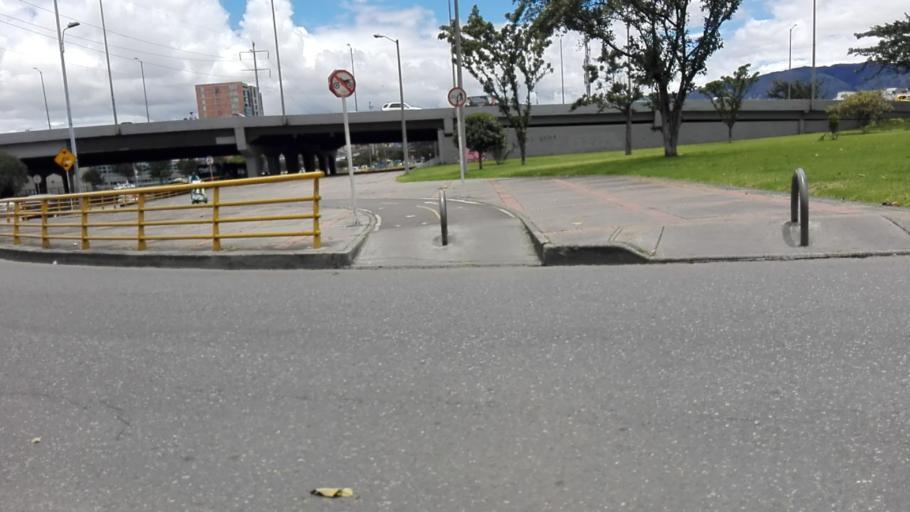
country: CO
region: Bogota D.C.
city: Barrio San Luis
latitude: 4.6830
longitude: -74.0796
